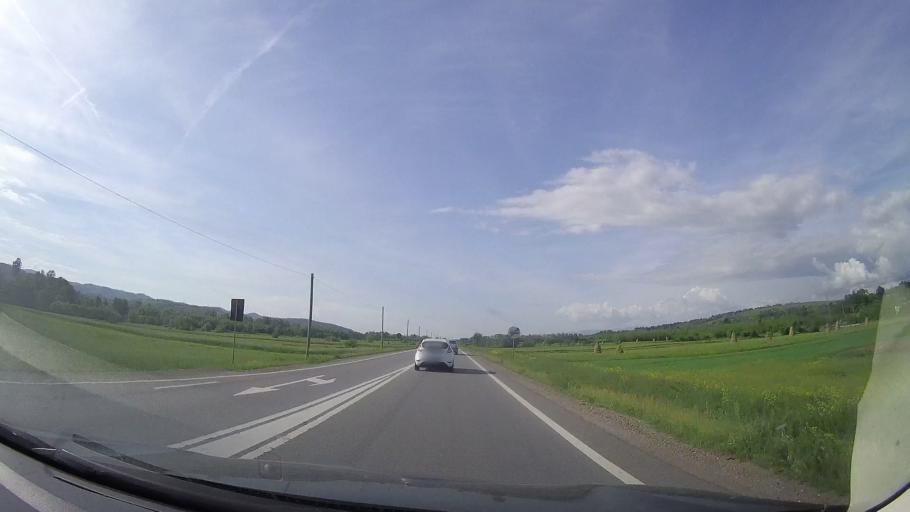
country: RO
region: Caras-Severin
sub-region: Comuna Bucosnita
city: Bucosnita
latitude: 45.3041
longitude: 22.2805
